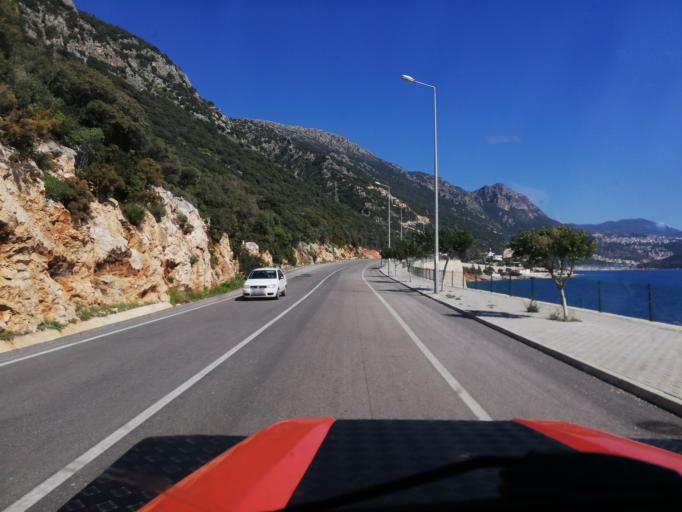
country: TR
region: Antalya
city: Kas
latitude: 36.2083
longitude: 29.6090
